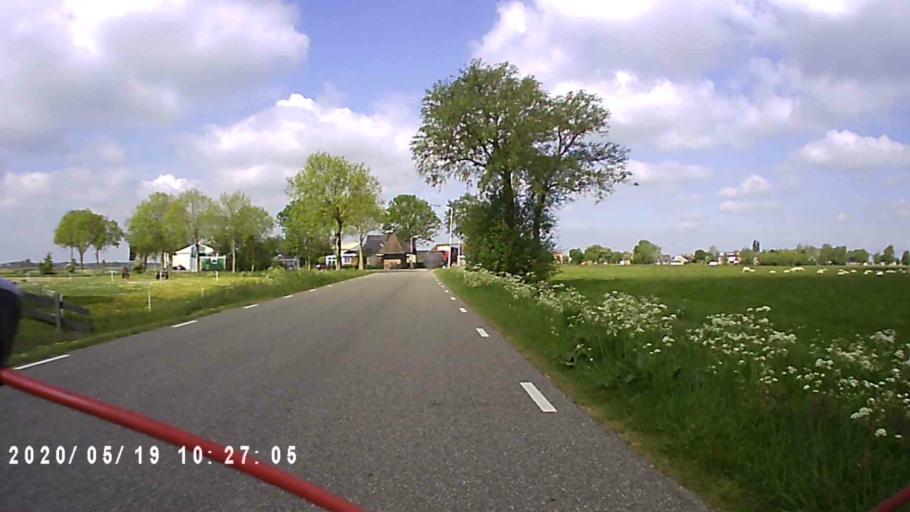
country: NL
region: Friesland
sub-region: Gemeente Kollumerland en Nieuwkruisland
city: Kollum
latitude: 53.3024
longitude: 6.1979
